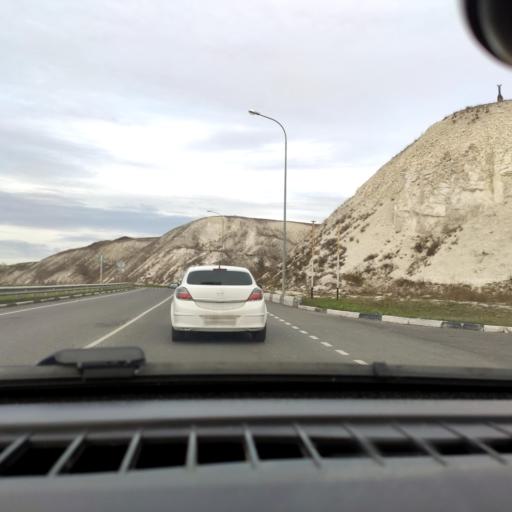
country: RU
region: Belgorod
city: Alekseyevka
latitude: 50.6399
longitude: 38.6669
